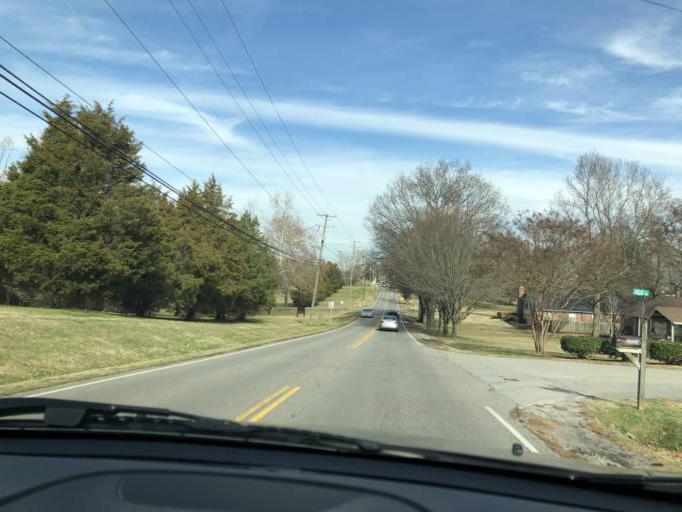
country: US
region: Tennessee
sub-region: Davidson County
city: Lakewood
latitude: 36.1909
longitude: -86.6740
